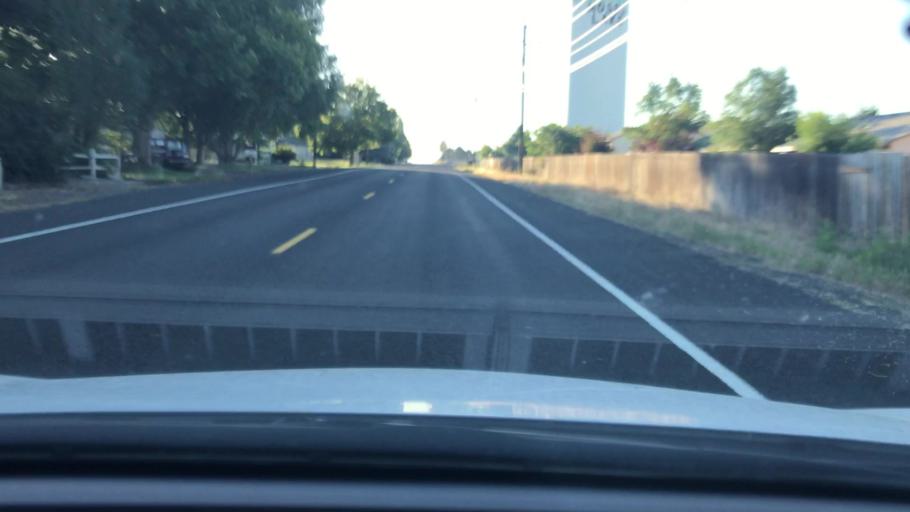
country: US
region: Washington
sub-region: Grant County
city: Moses Lake
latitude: 47.1164
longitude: -119.2497
